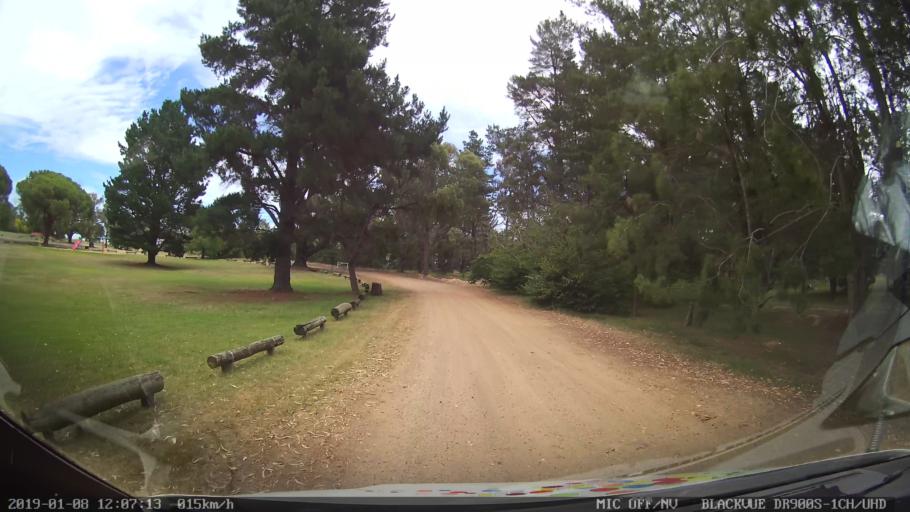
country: AU
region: New South Wales
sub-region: Armidale Dumaresq
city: Armidale
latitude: -30.4260
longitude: 151.5943
